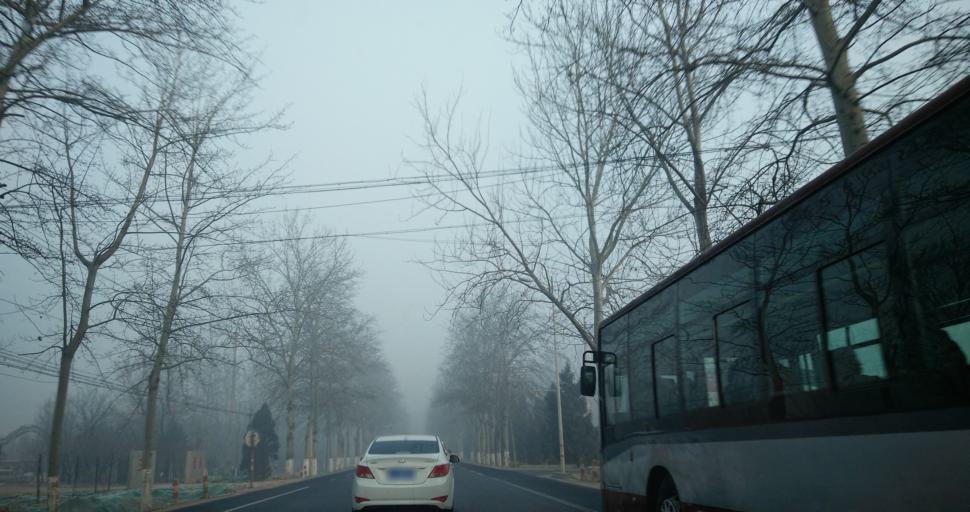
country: CN
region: Beijing
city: Yinghai
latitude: 39.7437
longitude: 116.4483
